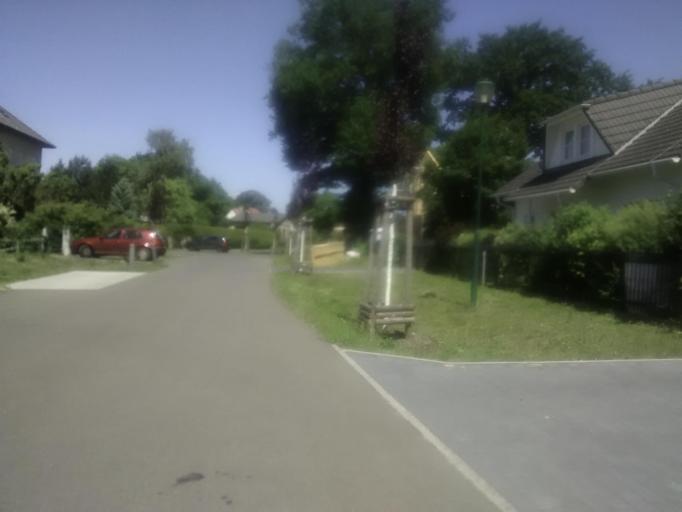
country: DE
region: Brandenburg
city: Hohen Neuendorf
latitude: 52.6645
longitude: 13.2780
